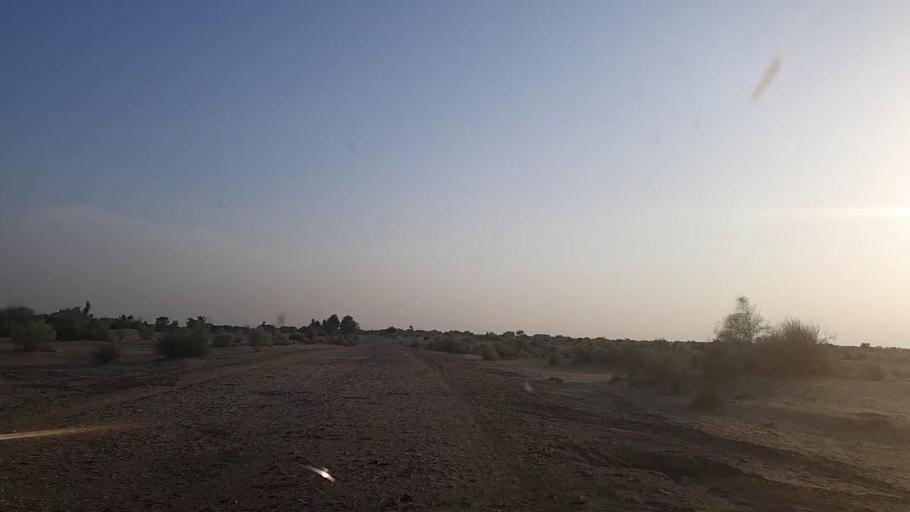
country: PK
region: Sindh
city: Khanpur
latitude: 27.6403
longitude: 69.4538
